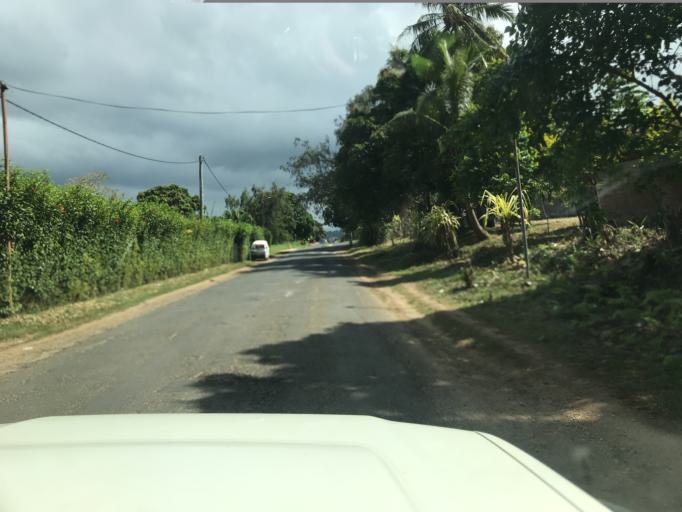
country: VU
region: Sanma
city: Luganville
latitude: -15.5104
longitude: 167.1856
